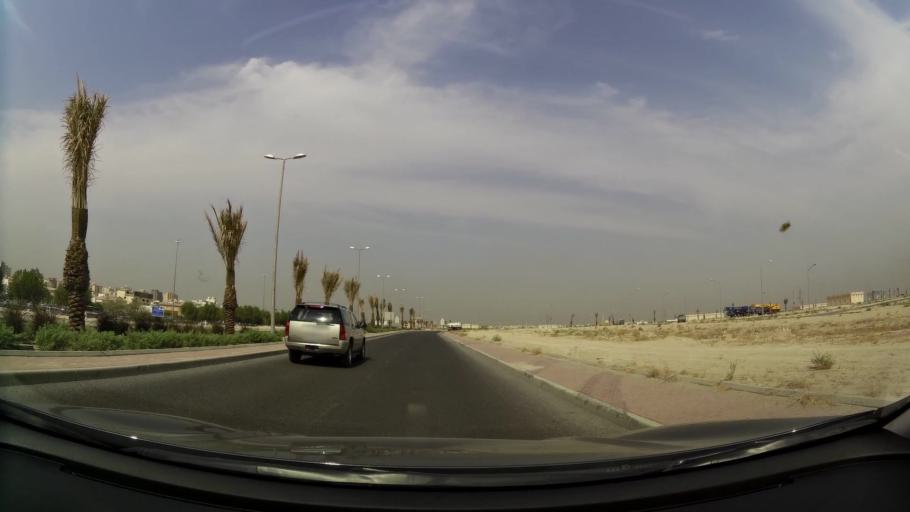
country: KW
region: Al Farwaniyah
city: Janub as Surrah
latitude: 29.2923
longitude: 47.9836
